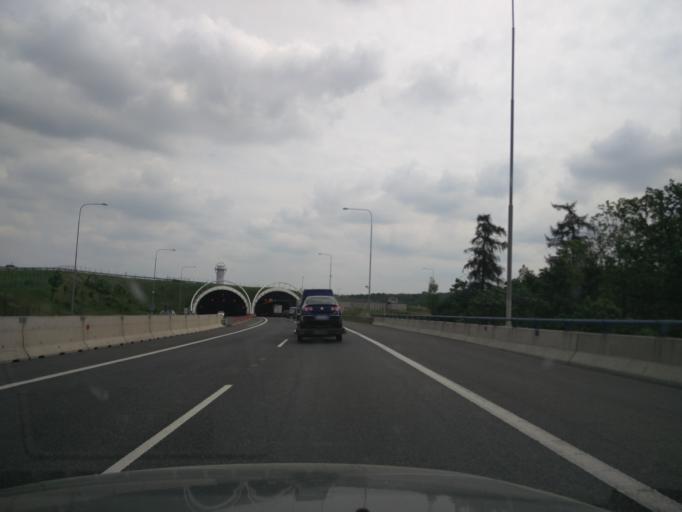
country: CZ
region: Central Bohemia
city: Cernosice
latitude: 49.9987
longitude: 14.3530
